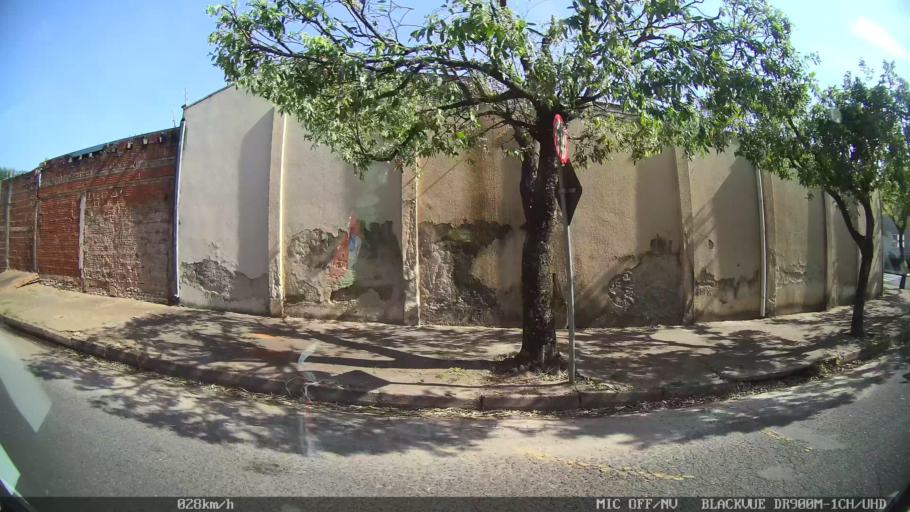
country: BR
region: Sao Paulo
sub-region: Sao Jose Do Rio Preto
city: Sao Jose do Rio Preto
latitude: -20.7916
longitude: -49.4267
